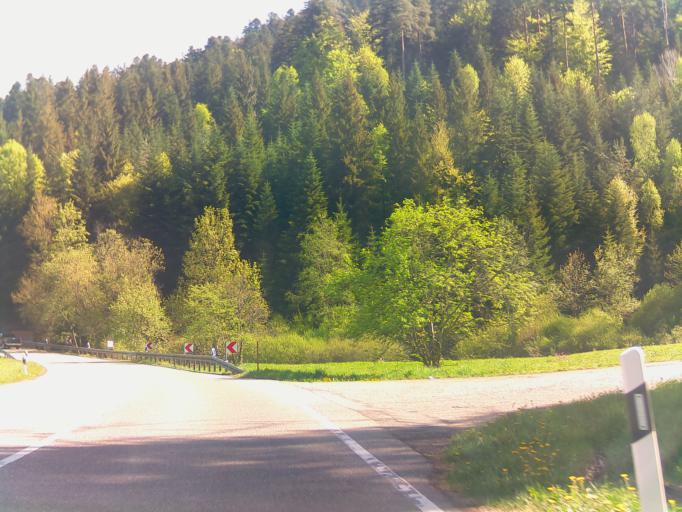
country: DE
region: Baden-Wuerttemberg
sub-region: Karlsruhe Region
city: Bad Wildbad
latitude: 48.7264
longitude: 8.5707
